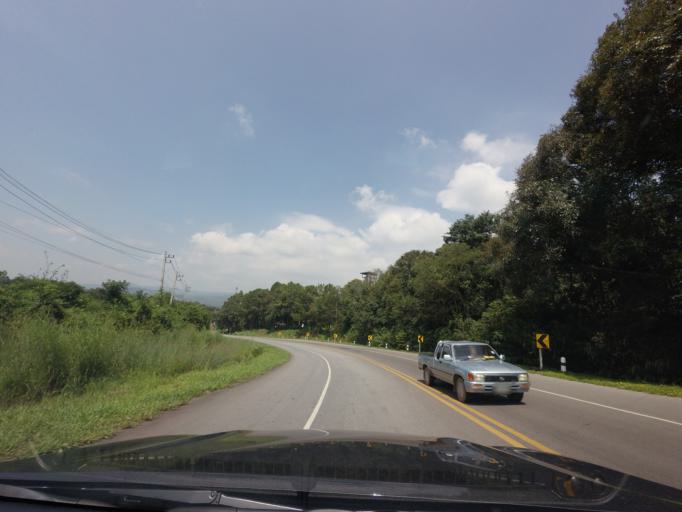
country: TH
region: Loei
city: Phu Ruea
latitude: 17.4589
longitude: 101.4136
